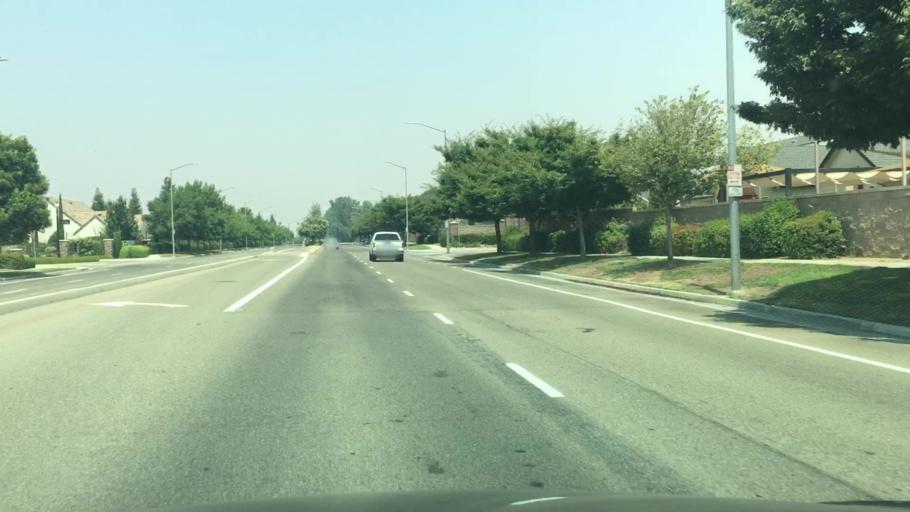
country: US
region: California
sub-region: Fresno County
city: Clovis
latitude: 36.8629
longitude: -119.7110
